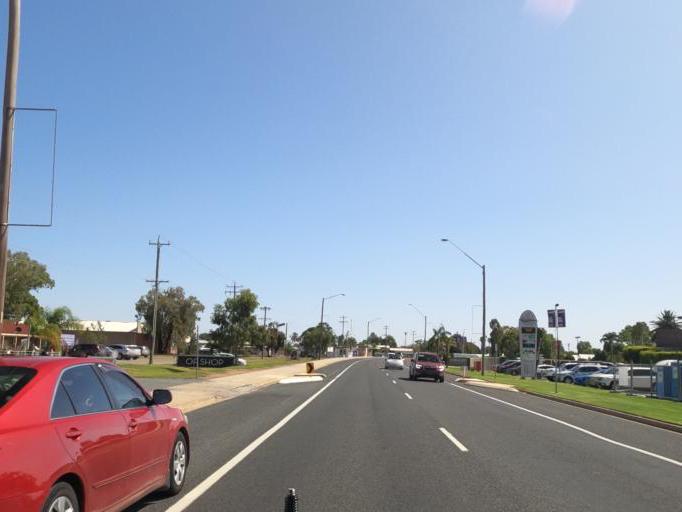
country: AU
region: New South Wales
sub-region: Corowa Shire
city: Mulwala
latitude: -35.9957
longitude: 146.0010
